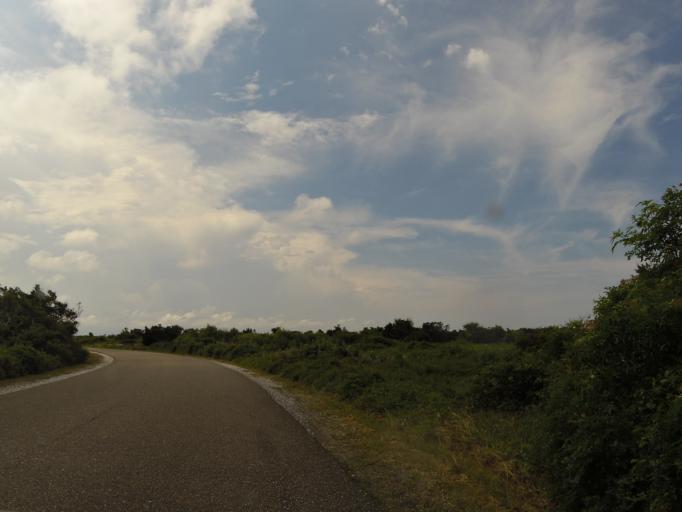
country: US
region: Florida
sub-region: Duval County
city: Atlantic Beach
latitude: 30.4361
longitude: -81.4118
